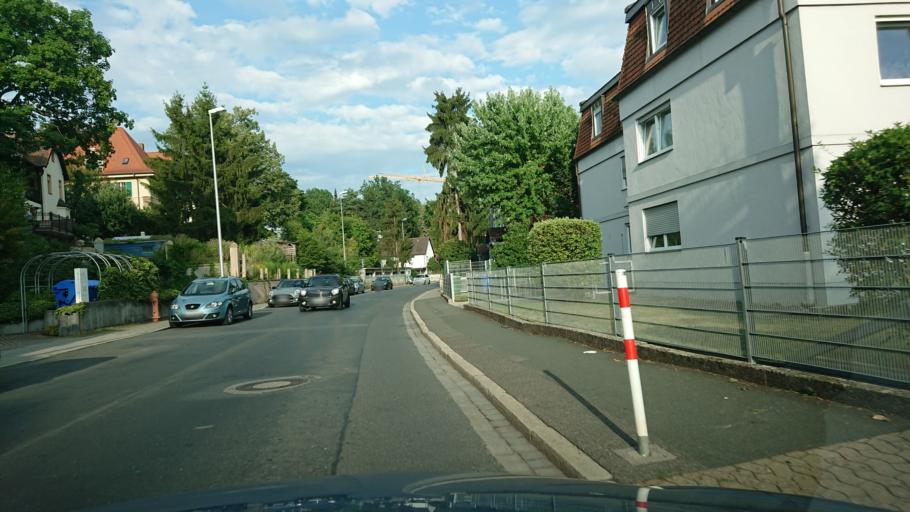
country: DE
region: Bavaria
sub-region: Regierungsbezirk Mittelfranken
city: Erlangen
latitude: 49.6064
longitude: 11.0100
